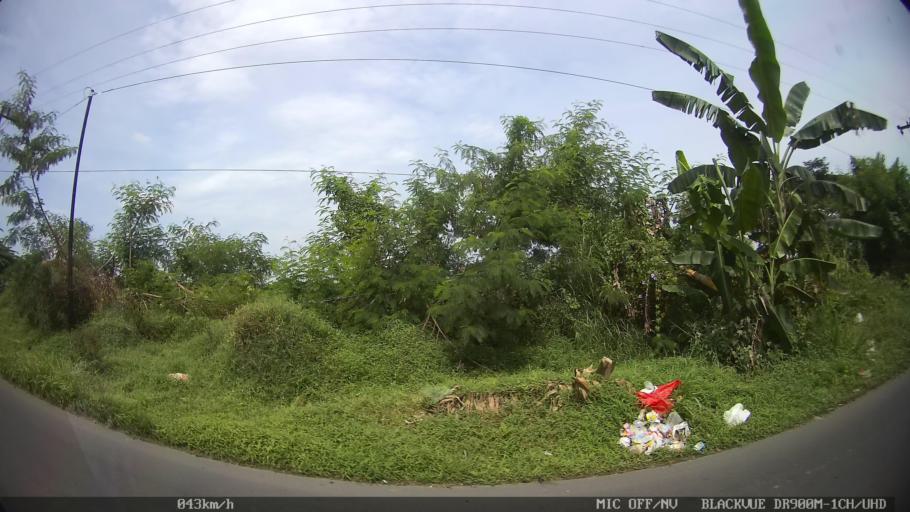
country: ID
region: North Sumatra
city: Medan
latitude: 3.6391
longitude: 98.7084
